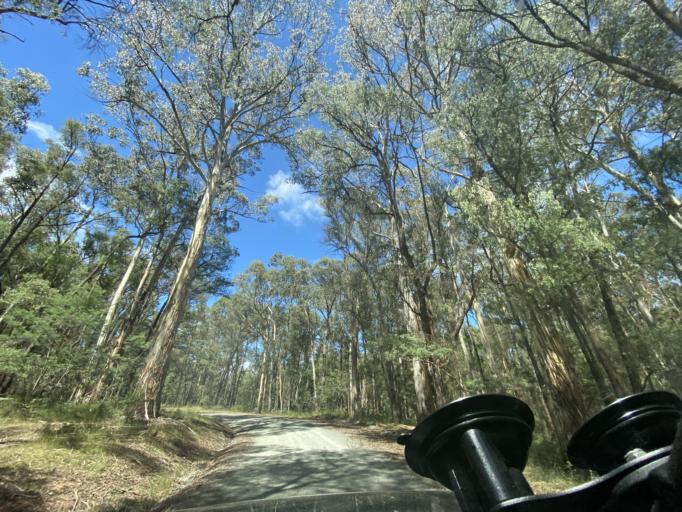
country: AU
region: Victoria
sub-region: Yarra Ranges
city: Millgrove
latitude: -37.5262
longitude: 146.0122
